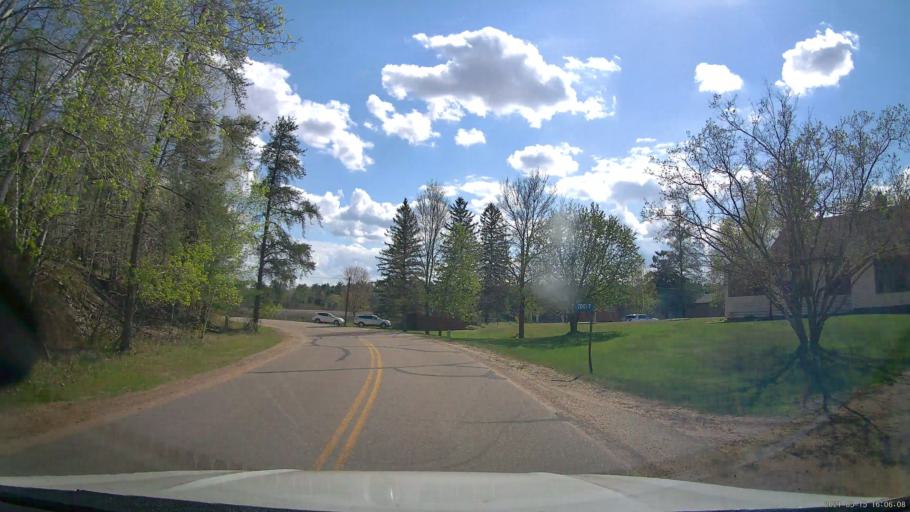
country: US
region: Minnesota
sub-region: Hubbard County
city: Park Rapids
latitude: 46.9812
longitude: -94.9519
